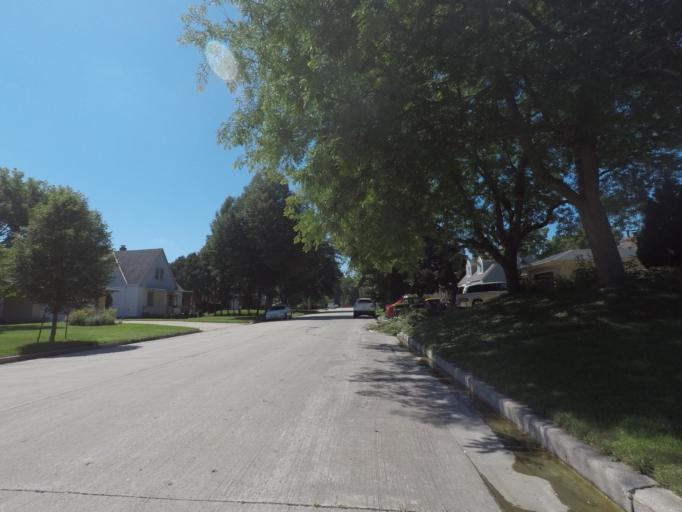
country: US
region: Wisconsin
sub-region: Waukesha County
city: Elm Grove
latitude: 43.0178
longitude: -88.0636
